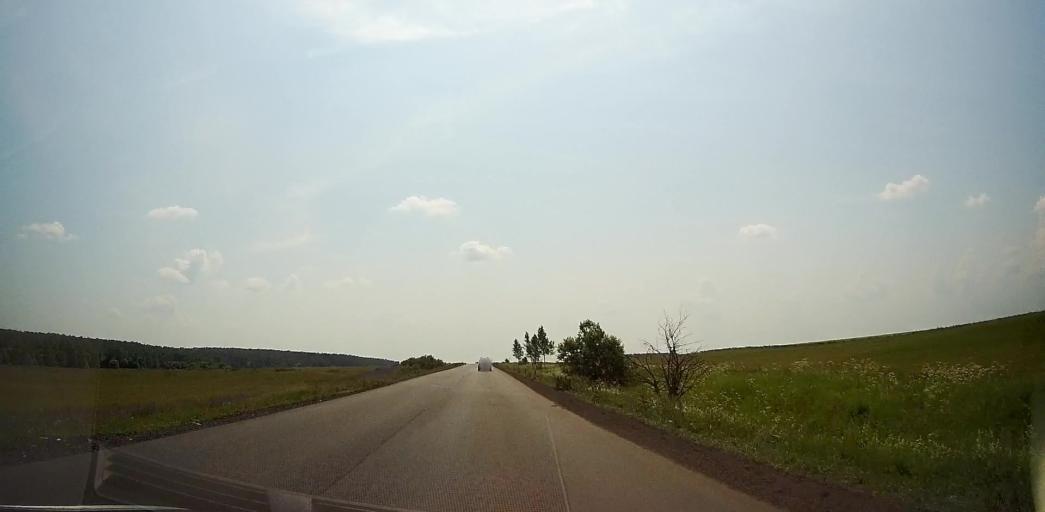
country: RU
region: Moskovskaya
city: Bronnitsy
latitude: 55.2923
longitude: 38.2136
